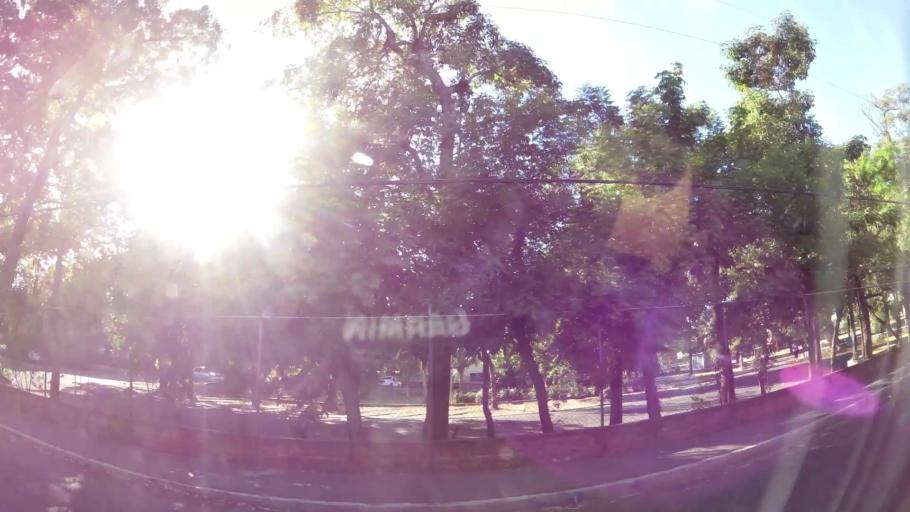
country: SV
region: San Miguel
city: San Miguel
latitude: 13.4721
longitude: -88.1875
